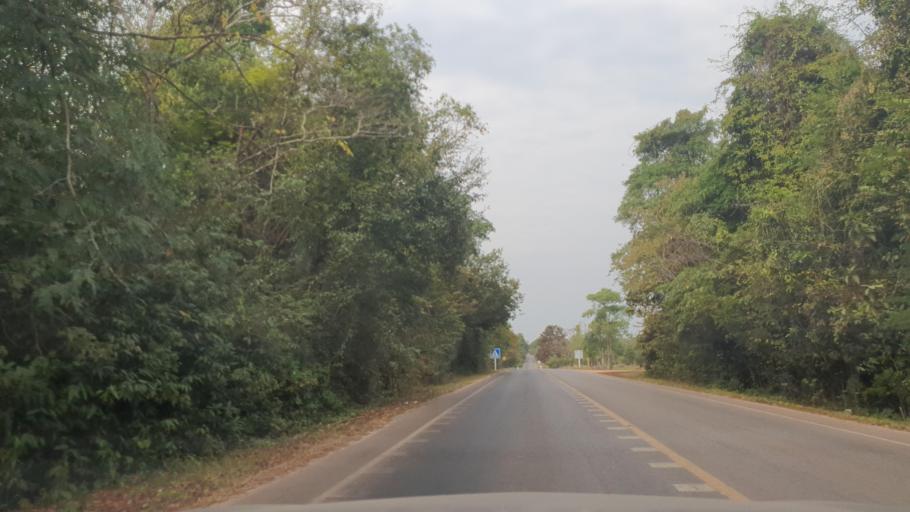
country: TH
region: Changwat Bueng Kan
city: Bung Khla
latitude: 18.2385
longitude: 104.0242
